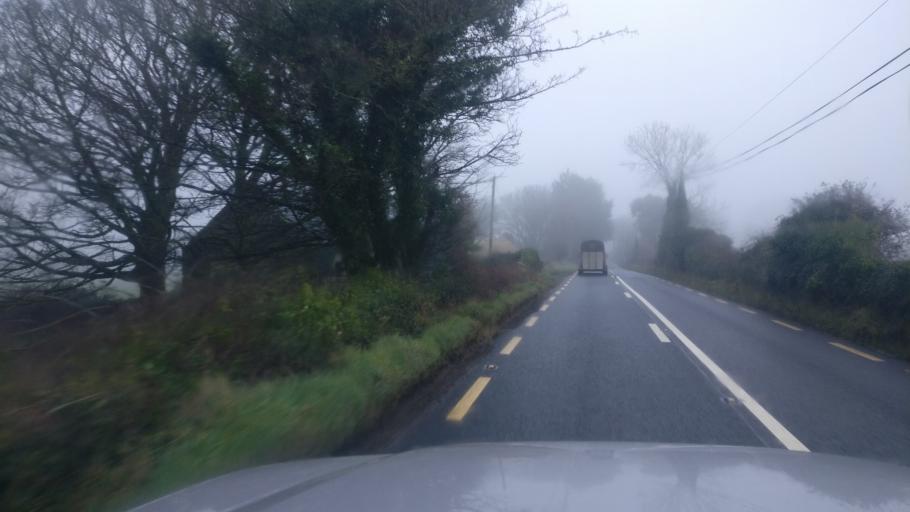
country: IE
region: Connaught
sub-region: County Galway
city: Loughrea
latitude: 53.1734
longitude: -8.6621
